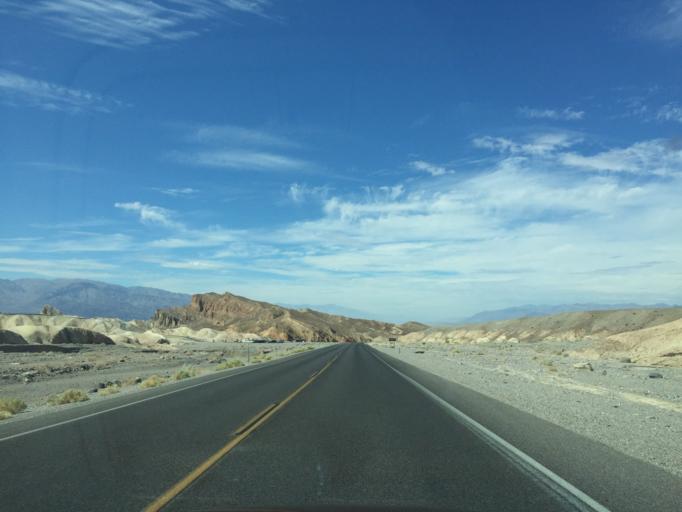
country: US
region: Nevada
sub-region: Nye County
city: Beatty
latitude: 36.4187
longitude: -116.8060
